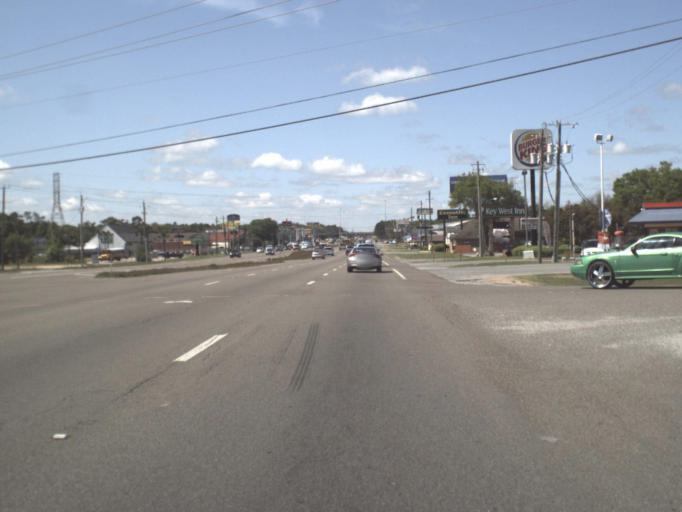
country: US
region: Florida
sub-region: Escambia County
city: Ensley
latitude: 30.4903
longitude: -87.2601
